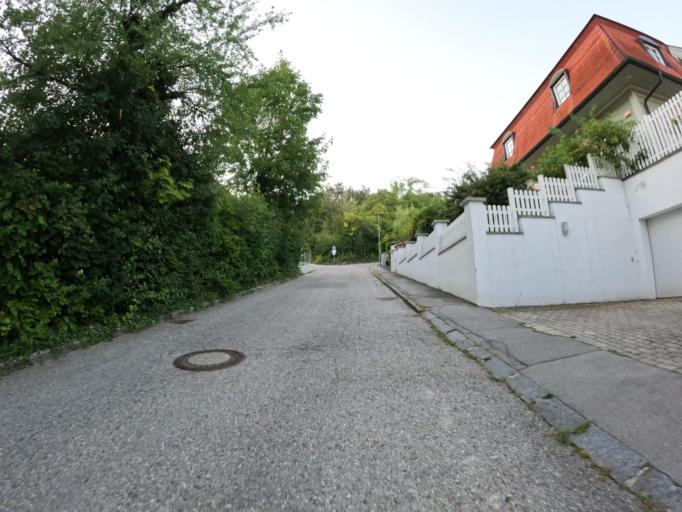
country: AT
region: Lower Austria
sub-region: Politischer Bezirk Baden
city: Baden
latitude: 48.0104
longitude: 16.2159
